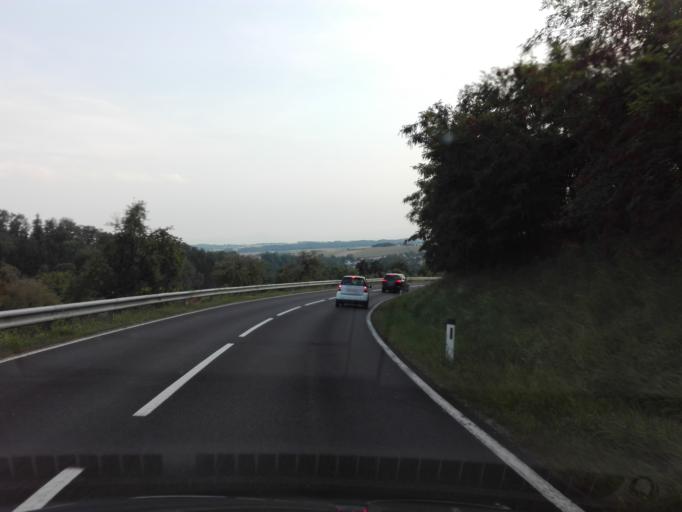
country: AT
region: Upper Austria
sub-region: Politischer Bezirk Grieskirchen
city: Grieskirchen
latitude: 48.2592
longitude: 13.8142
